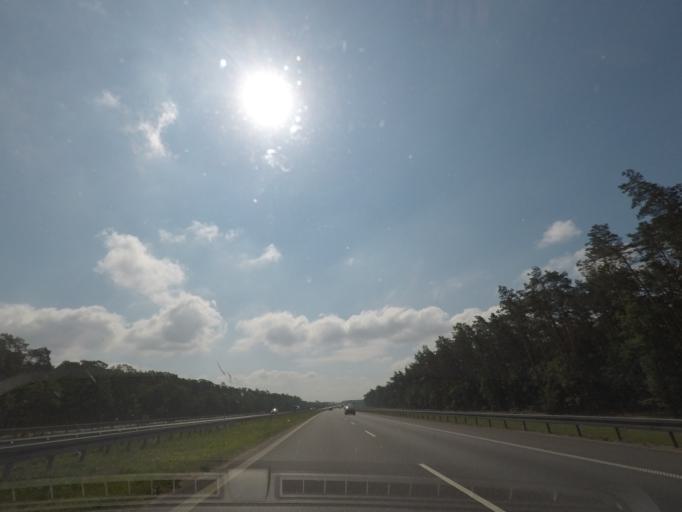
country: PL
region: Kujawsko-Pomorskie
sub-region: Powiat aleksandrowski
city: Aleksandrow Kujawski
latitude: 52.8803
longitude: 18.7423
